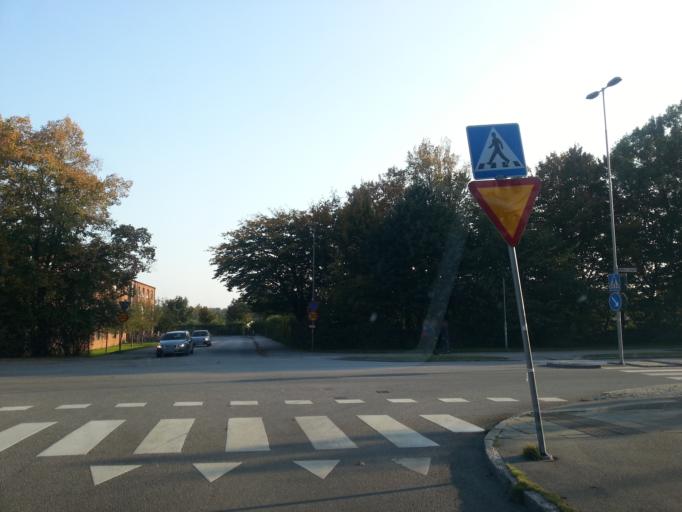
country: SE
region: Skane
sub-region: Lunds Kommun
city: Lund
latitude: 55.6958
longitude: 13.1992
